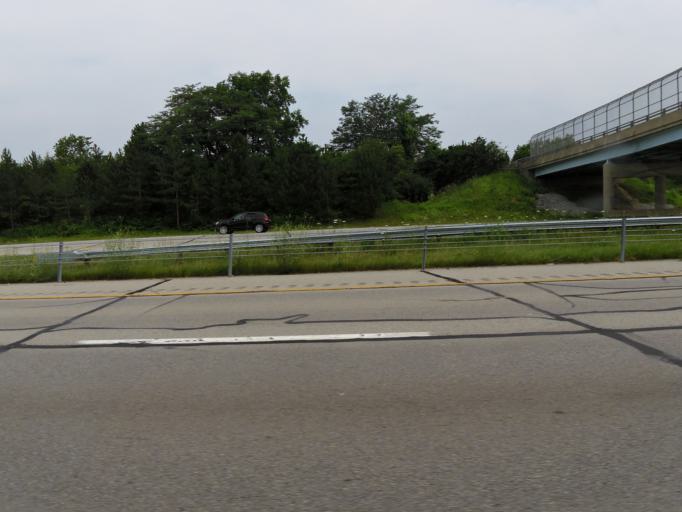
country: US
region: Ohio
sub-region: Montgomery County
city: Centerville
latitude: 39.6486
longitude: -84.1486
